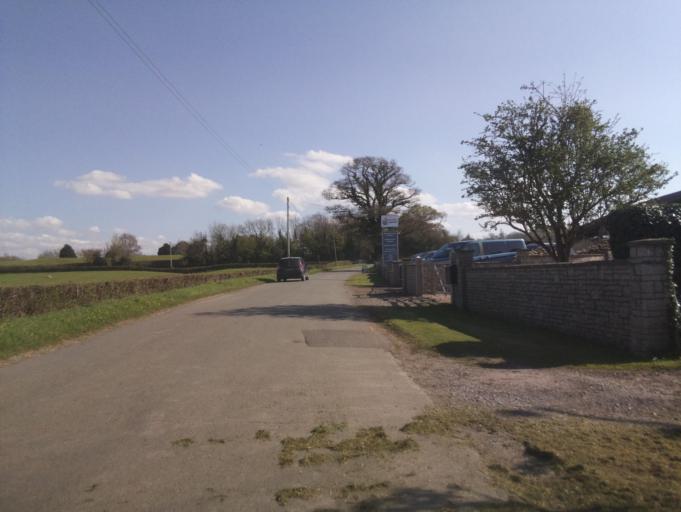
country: GB
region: England
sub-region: South Gloucestershire
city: Thornbury
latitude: 51.6155
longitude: -2.5550
